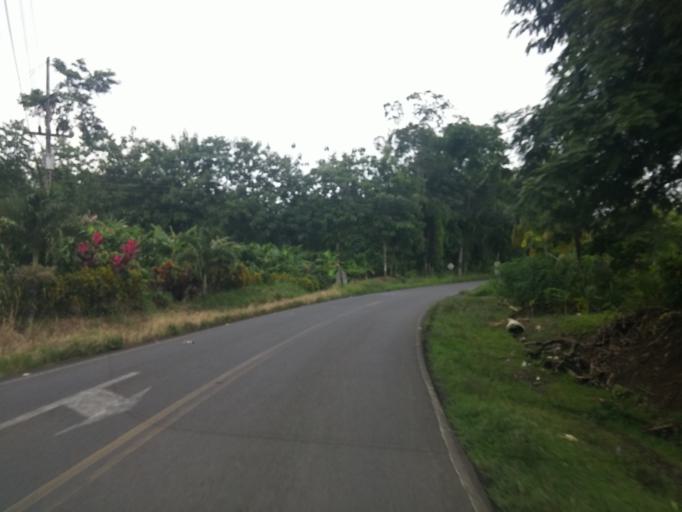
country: CR
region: Alajuela
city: Upala
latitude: 10.8130
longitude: -85.0221
